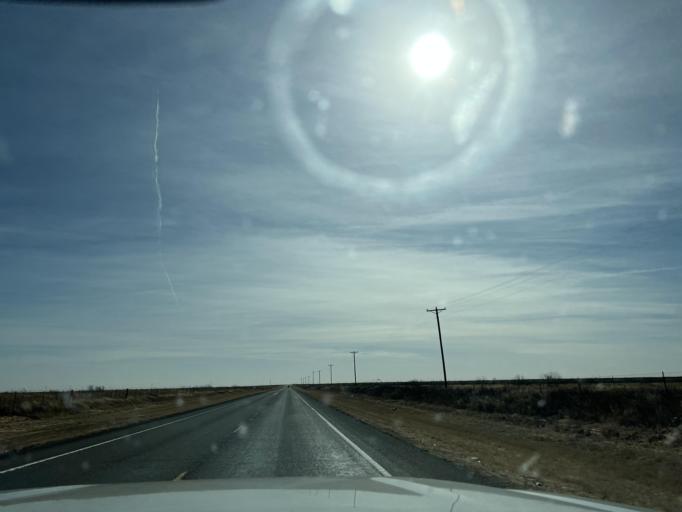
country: US
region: Texas
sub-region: Andrews County
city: Andrews
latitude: 32.4135
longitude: -102.4309
